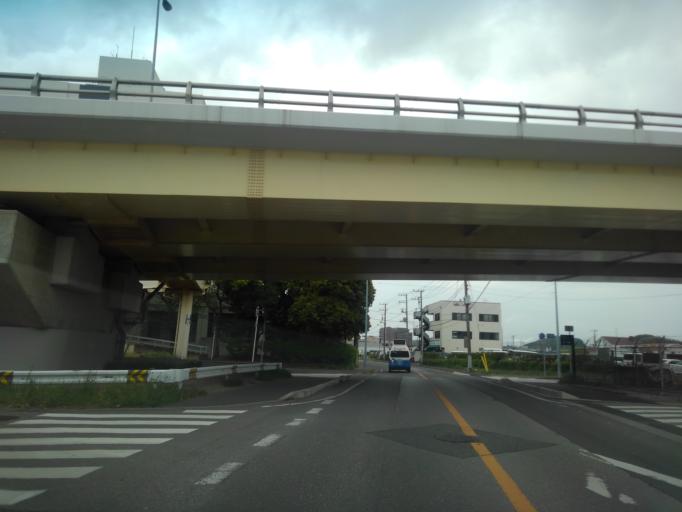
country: JP
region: Chiba
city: Kimitsu
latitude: 35.3305
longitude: 139.9035
